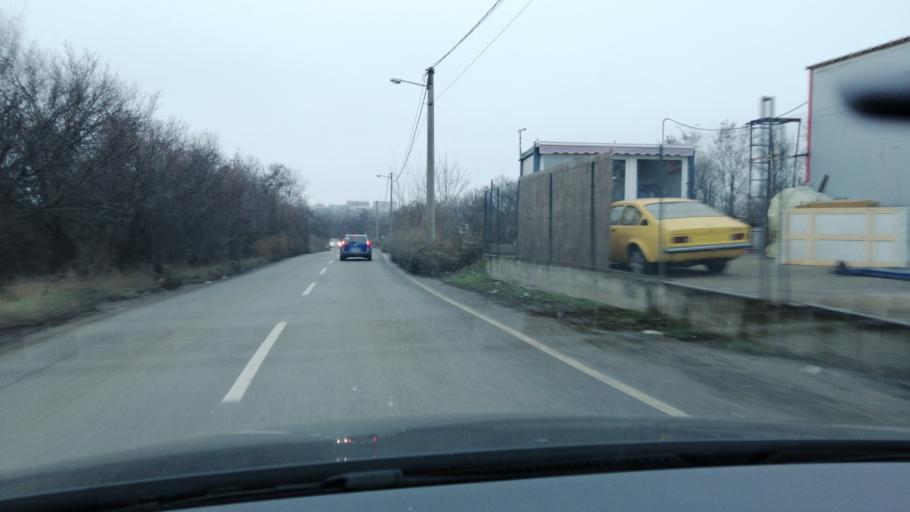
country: RS
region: Central Serbia
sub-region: Belgrade
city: Zvezdara
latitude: 44.7822
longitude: 20.5481
